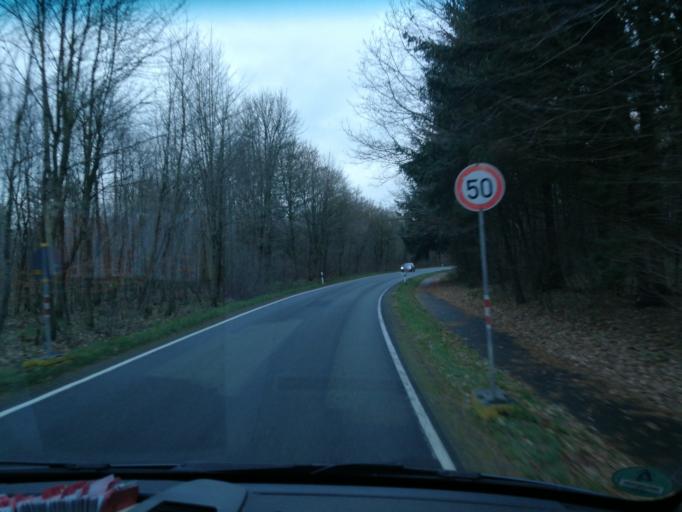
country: DE
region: Schleswig-Holstein
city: Handewitt
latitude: 54.7894
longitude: 9.3163
